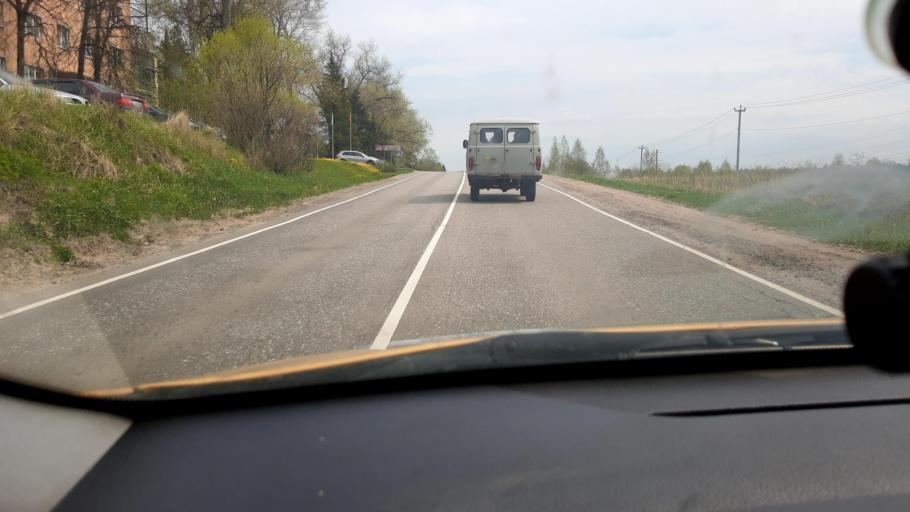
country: RU
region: Moskovskaya
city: Kostrovo
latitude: 55.8724
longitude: 36.6188
